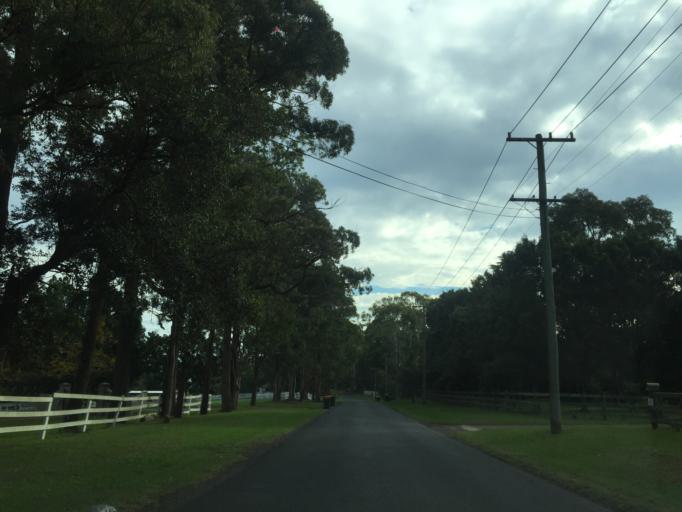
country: AU
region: New South Wales
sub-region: Hornsby Shire
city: Galston
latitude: -33.6473
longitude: 151.0716
